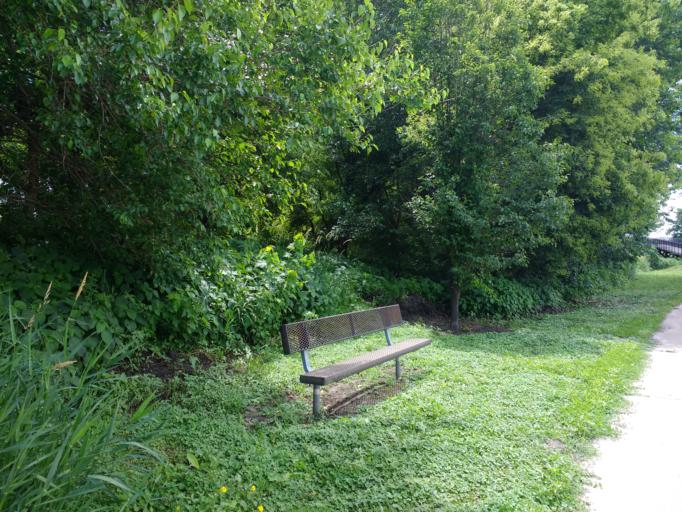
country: US
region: Iowa
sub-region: Plymouth County
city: Kingsley
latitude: 42.4694
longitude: -95.7903
